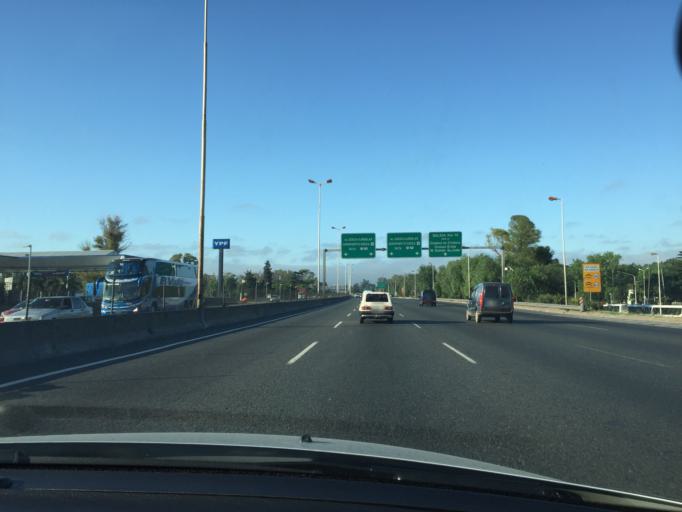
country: AR
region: Buenos Aires F.D.
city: Villa Lugano
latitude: -34.7139
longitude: -58.5076
